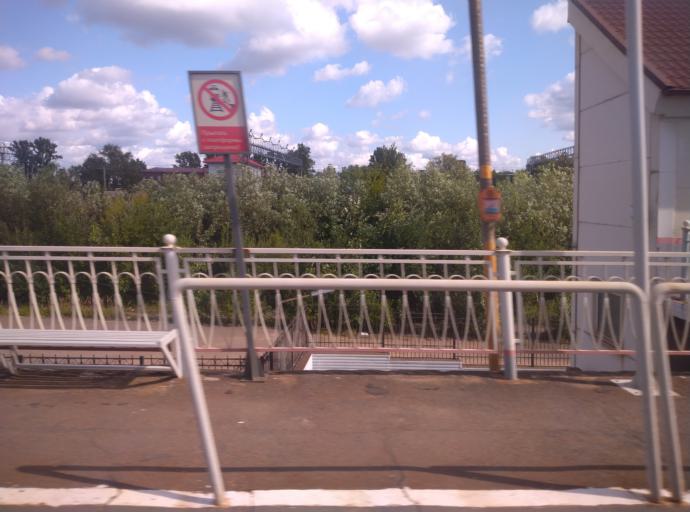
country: RU
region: St.-Petersburg
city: Obukhovo
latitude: 59.8670
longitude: 30.4250
